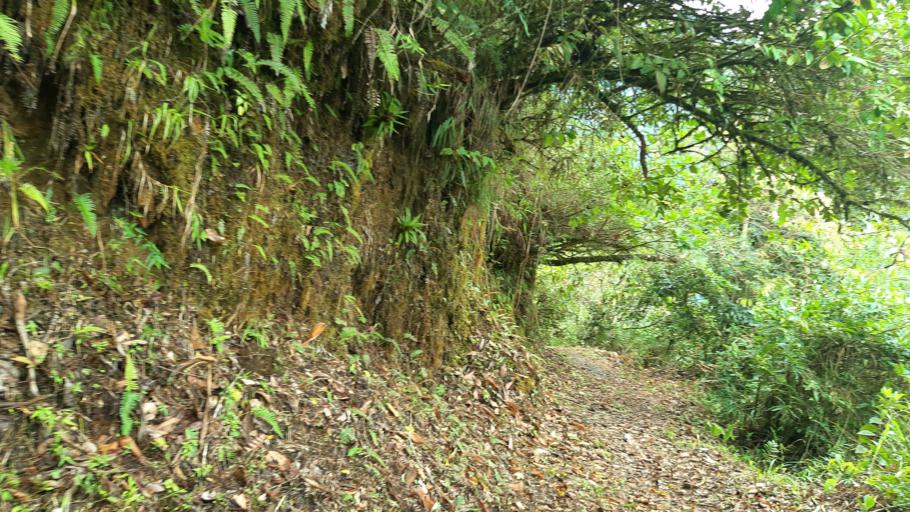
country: CO
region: Boyaca
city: Santa Maria
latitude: 4.9113
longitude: -73.3012
